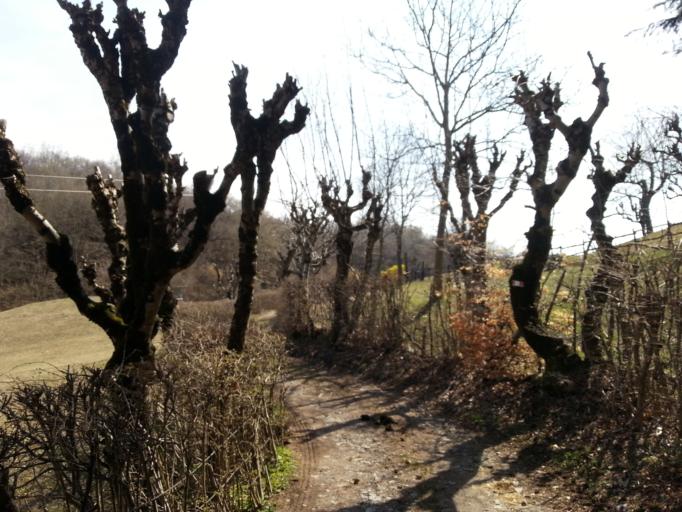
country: IT
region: Lombardy
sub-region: Provincia di Como
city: Grandola ed Uniti
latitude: 46.0063
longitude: 9.2122
